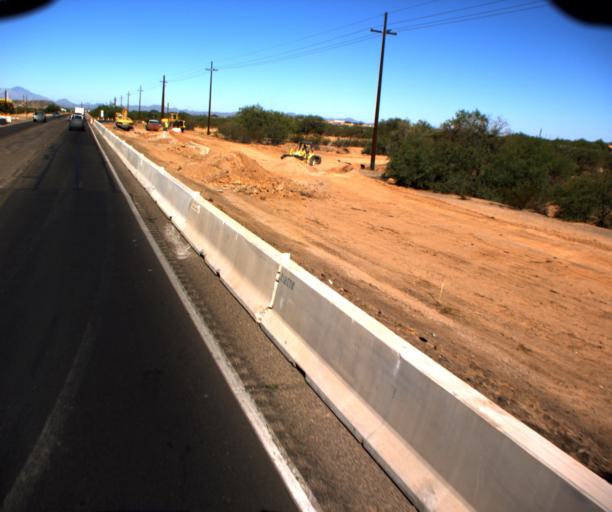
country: US
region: Arizona
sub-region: Pima County
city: Tucson Estates
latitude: 32.1678
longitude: -111.0843
